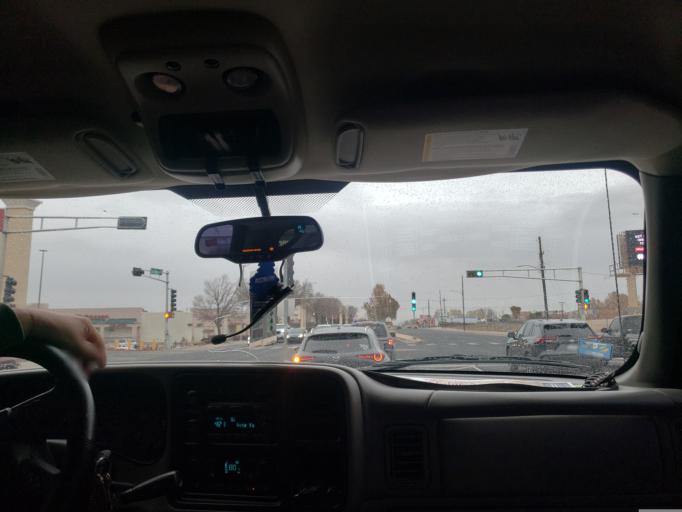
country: US
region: New Mexico
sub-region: Bernalillo County
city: North Valley
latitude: 35.1325
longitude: -106.5865
